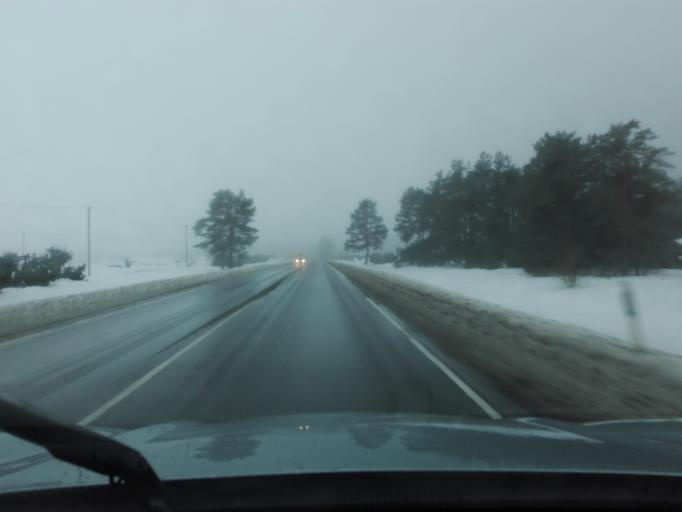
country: EE
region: Harju
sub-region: Saku vald
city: Saku
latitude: 59.3009
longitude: 24.7400
